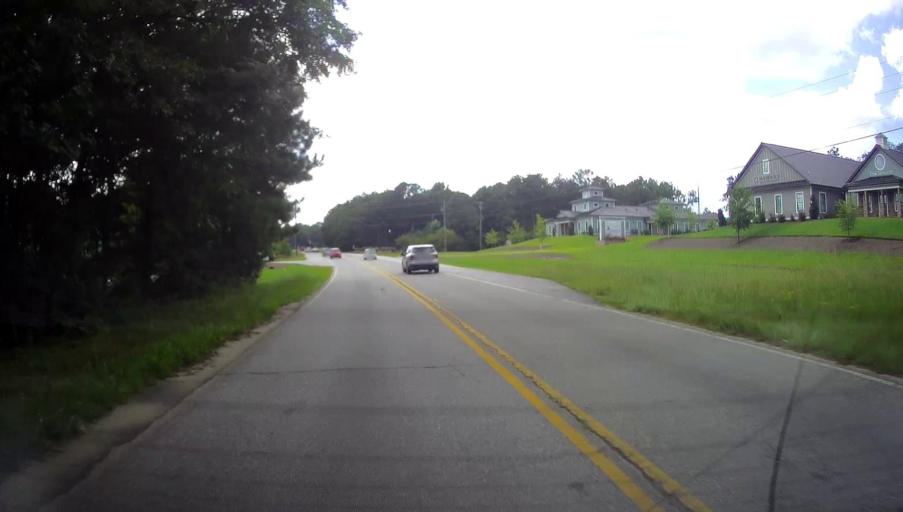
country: US
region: Alabama
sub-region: Russell County
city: Phenix City
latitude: 32.5646
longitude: -84.9432
